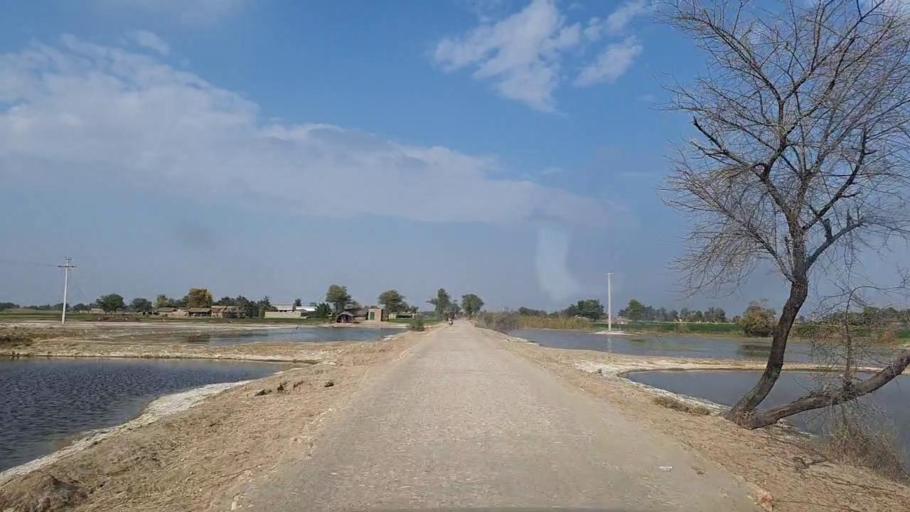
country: PK
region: Sindh
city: Sanghar
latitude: 26.2354
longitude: 69.0195
